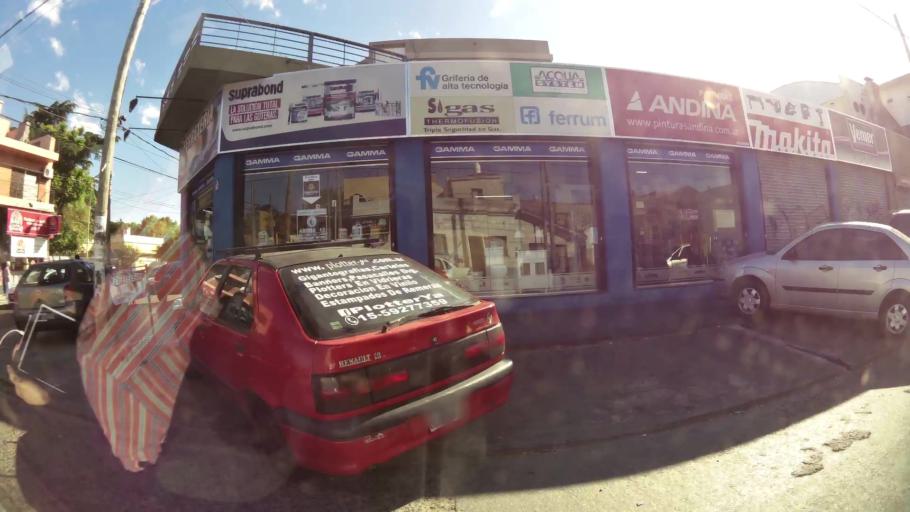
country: AR
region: Buenos Aires
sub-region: Partido de General San Martin
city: General San Martin
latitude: -34.5364
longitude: -58.5613
